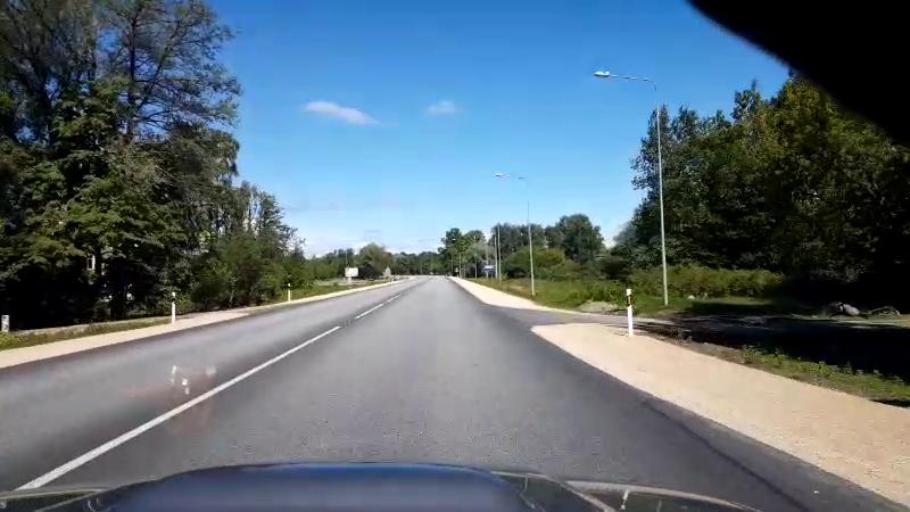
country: LV
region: Salacgrivas
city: Salacgriva
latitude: 57.7873
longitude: 24.3547
